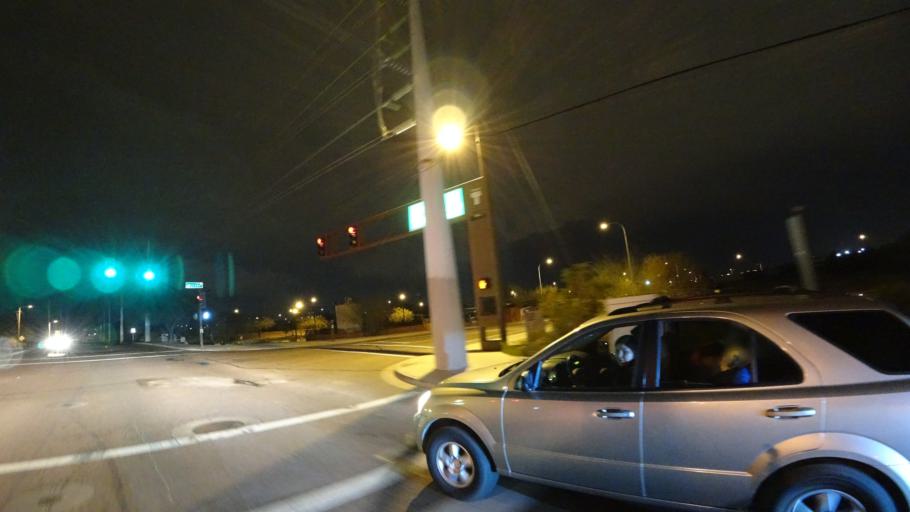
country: US
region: Arizona
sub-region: Maricopa County
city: Tempe
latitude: 33.4403
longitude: -111.9181
